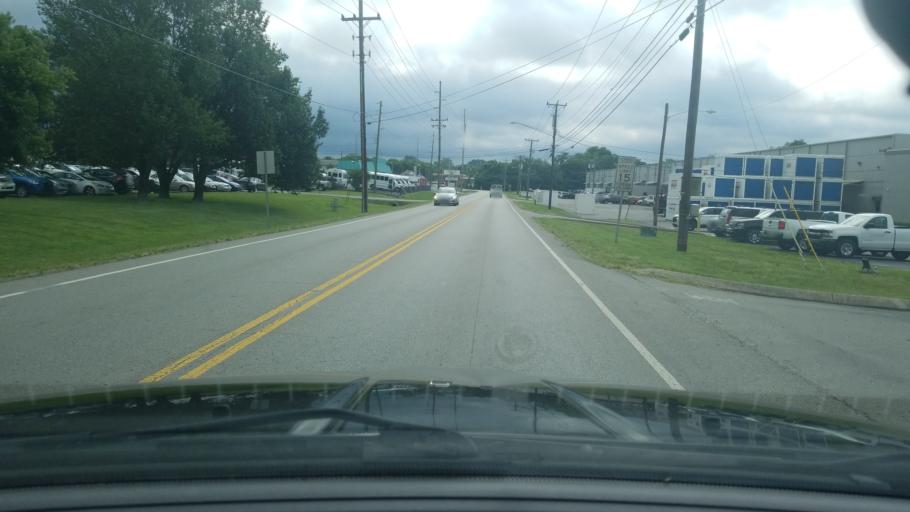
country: US
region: Tennessee
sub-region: Davidson County
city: Oak Hill
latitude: 36.0959
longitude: -86.7423
